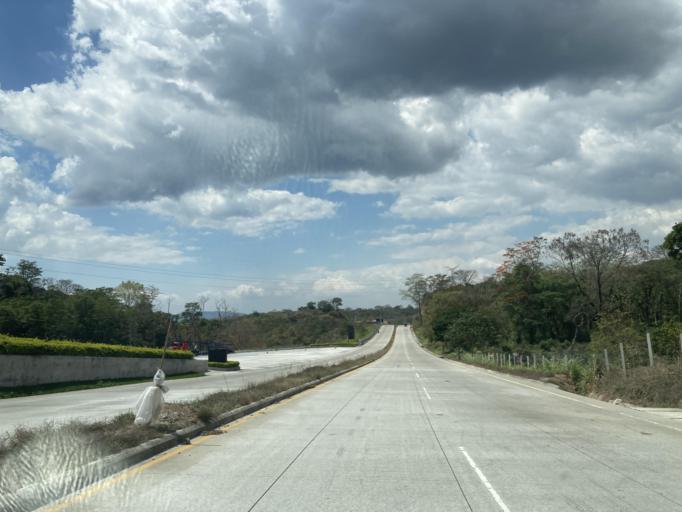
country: GT
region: Santa Rosa
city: Barberena
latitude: 14.3020
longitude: -90.3720
